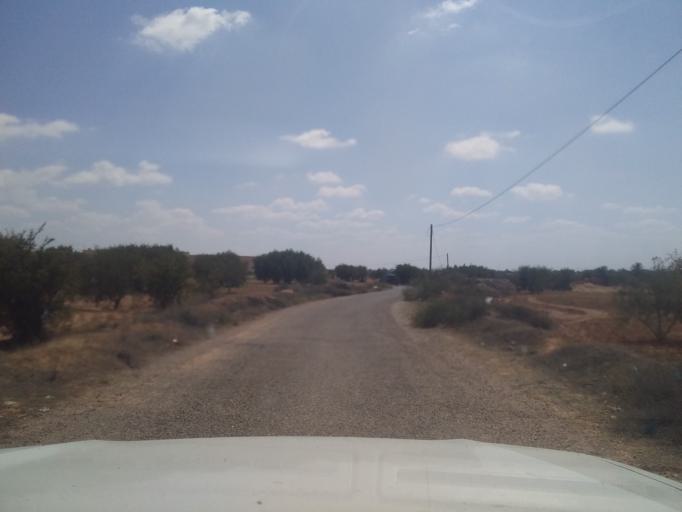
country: TN
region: Madanin
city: Medenine
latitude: 33.6109
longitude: 10.3091
